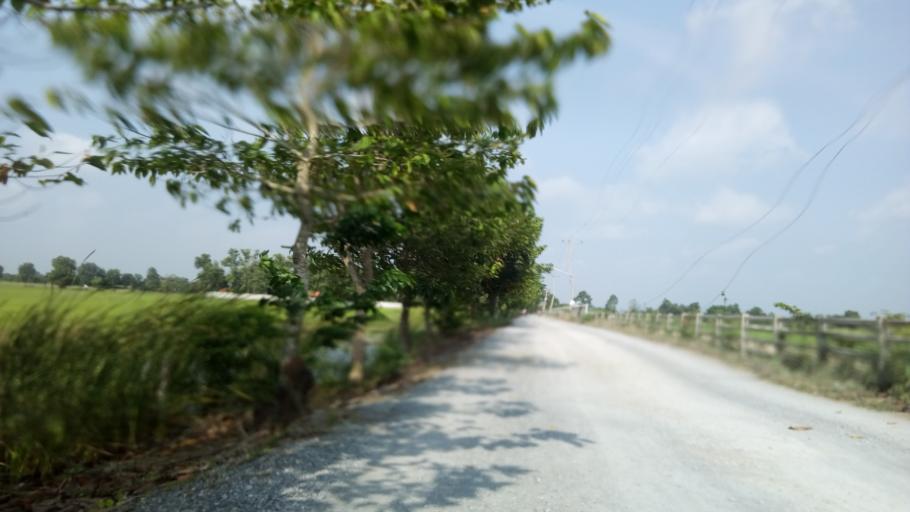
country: TH
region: Pathum Thani
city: Nong Suea
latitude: 14.1885
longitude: 100.8391
